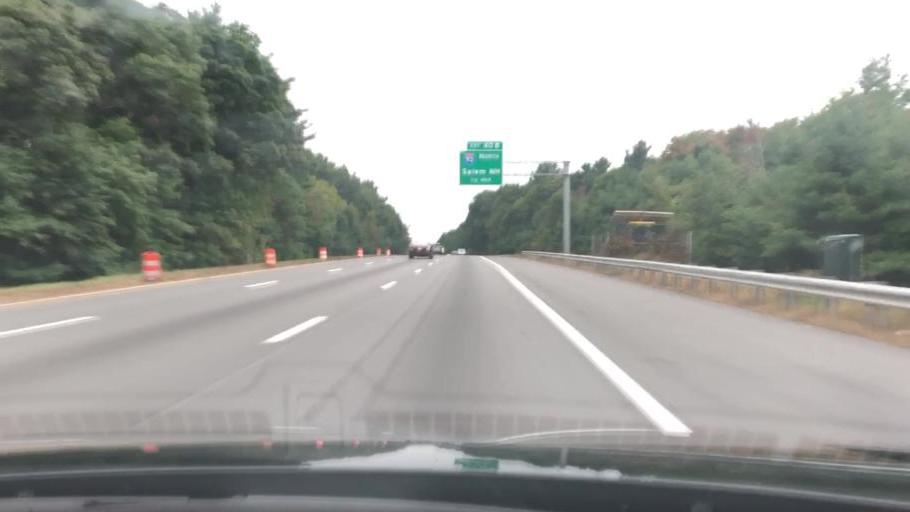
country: US
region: Massachusetts
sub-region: Essex County
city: Lawrence
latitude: 42.6708
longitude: -71.1842
